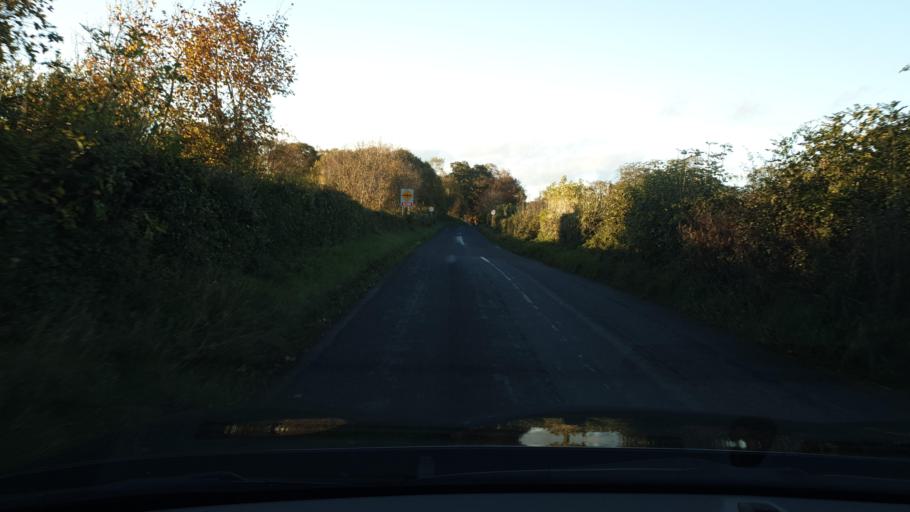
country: IE
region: Leinster
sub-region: Lu
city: Drogheda
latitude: 53.6911
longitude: -6.3416
